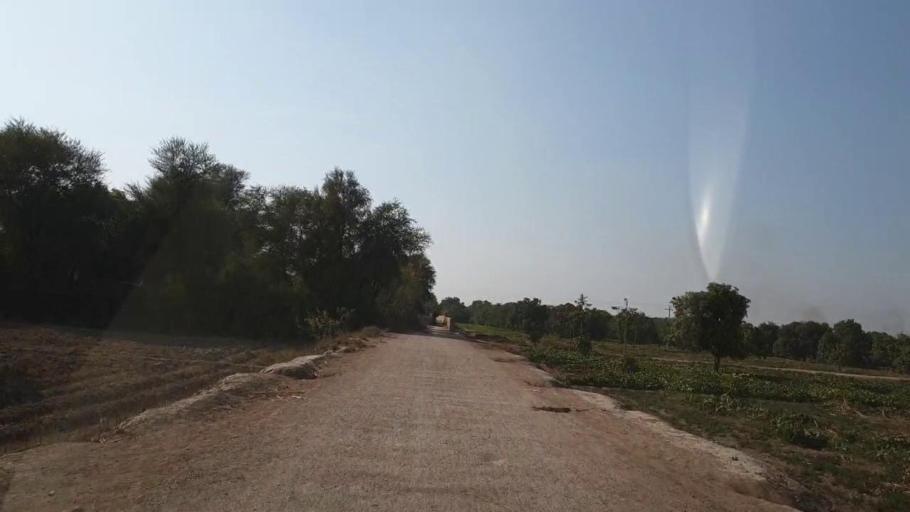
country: PK
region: Sindh
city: Tando Jam
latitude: 25.4870
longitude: 68.5364
